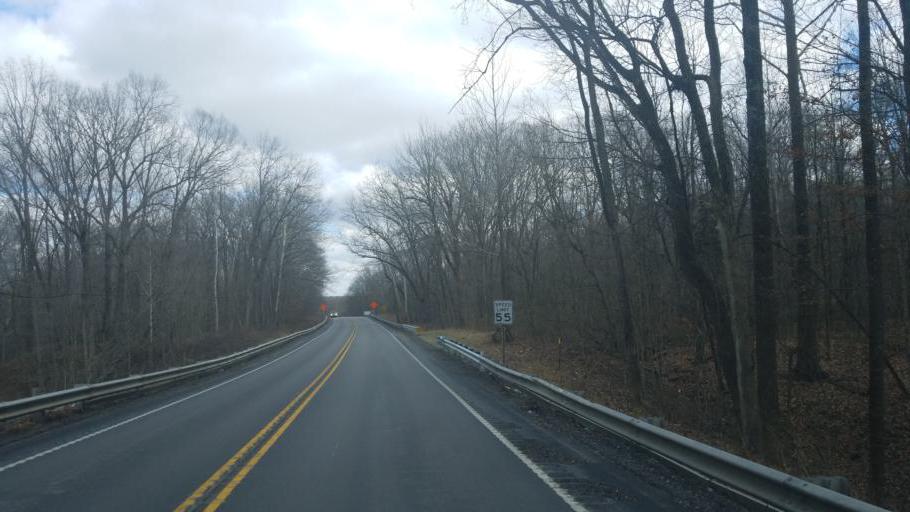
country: US
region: Indiana
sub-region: Parke County
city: Montezuma
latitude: 39.7903
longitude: -87.3913
